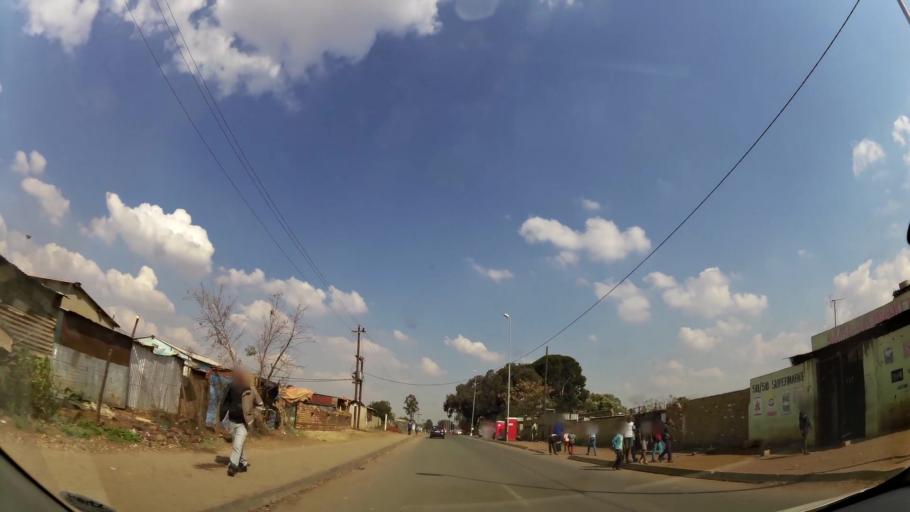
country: ZA
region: Gauteng
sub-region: Ekurhuleni Metropolitan Municipality
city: Germiston
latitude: -26.3163
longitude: 28.1450
